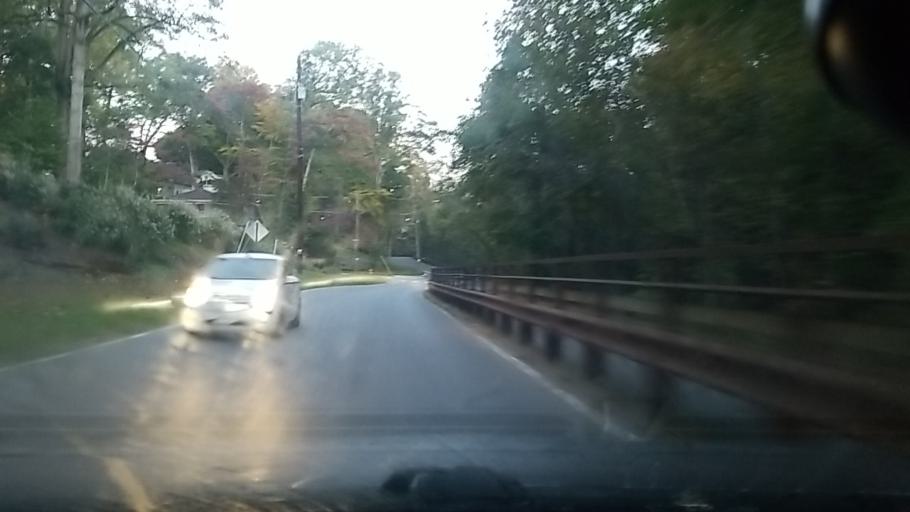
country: US
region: Maryland
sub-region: Montgomery County
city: Takoma Park
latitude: 38.9818
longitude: -76.9986
